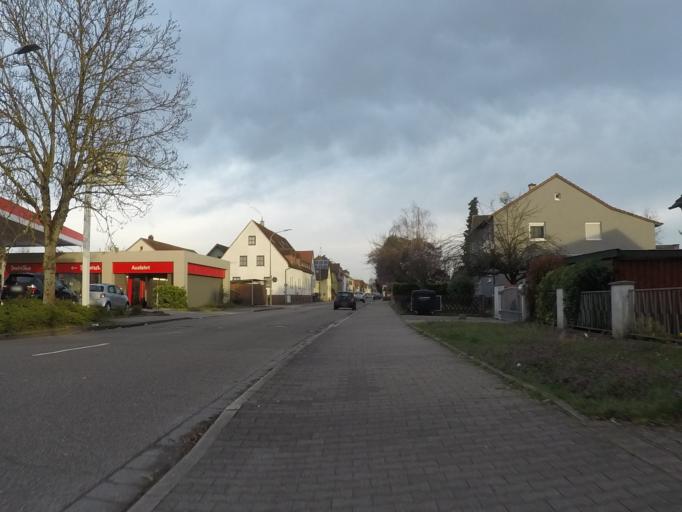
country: DE
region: Rheinland-Pfalz
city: Worth am Rhein
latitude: 49.0469
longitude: 8.2722
